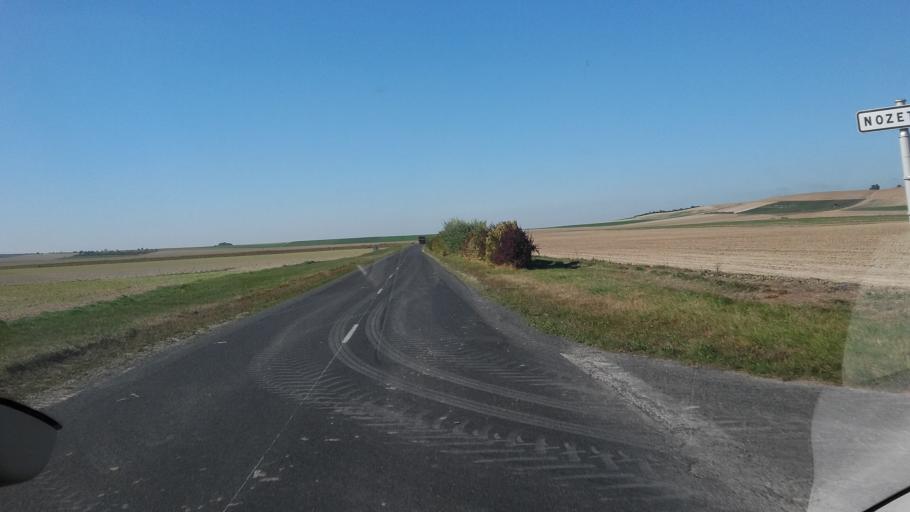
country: FR
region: Champagne-Ardenne
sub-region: Departement de la Marne
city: Connantre
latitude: 48.7456
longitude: 3.8904
